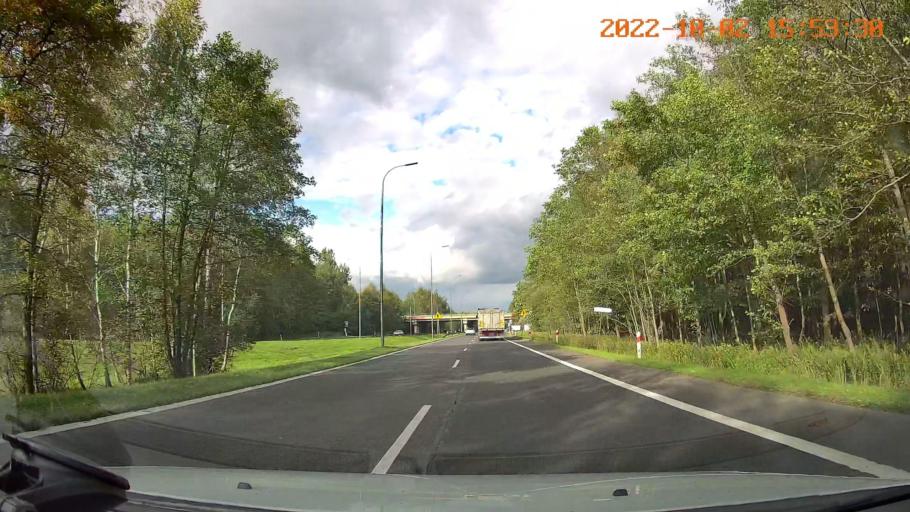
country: PL
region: Silesian Voivodeship
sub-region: Katowice
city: Murcki
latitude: 50.1688
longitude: 19.0186
